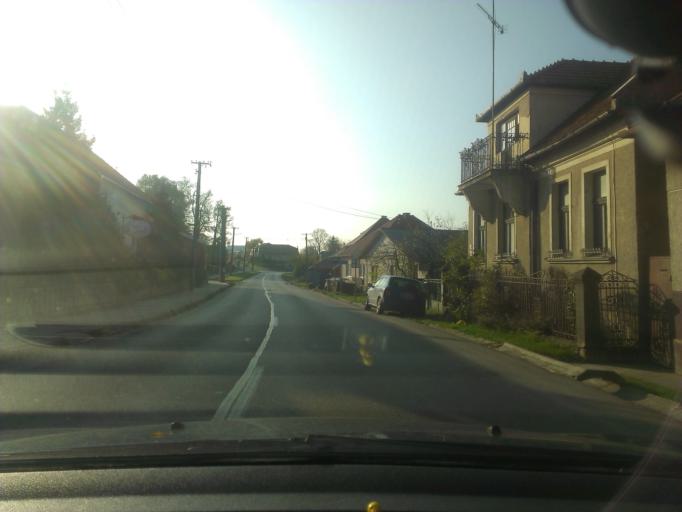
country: SK
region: Trnavsky
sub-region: Okres Trnava
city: Piestany
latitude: 48.5016
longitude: 17.9832
